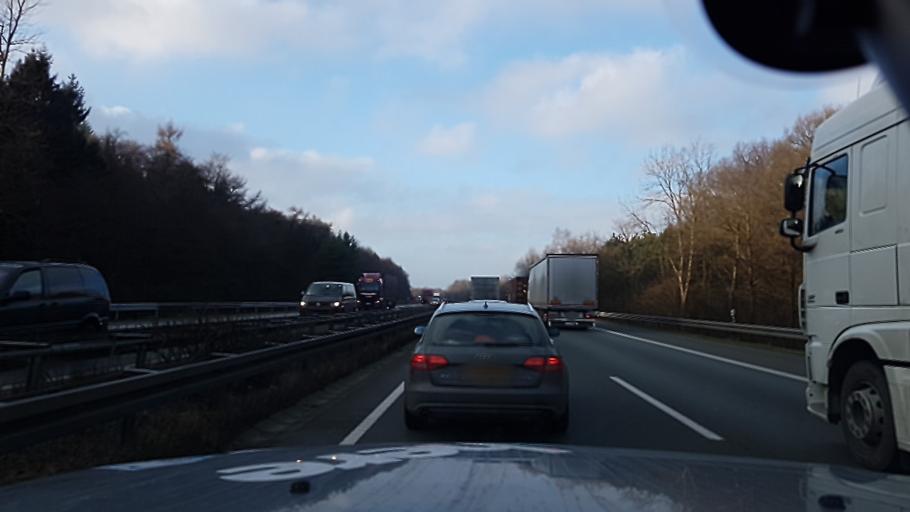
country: DE
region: North Rhine-Westphalia
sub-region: Regierungsbezirk Munster
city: Birgte
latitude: 52.2807
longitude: 7.6372
